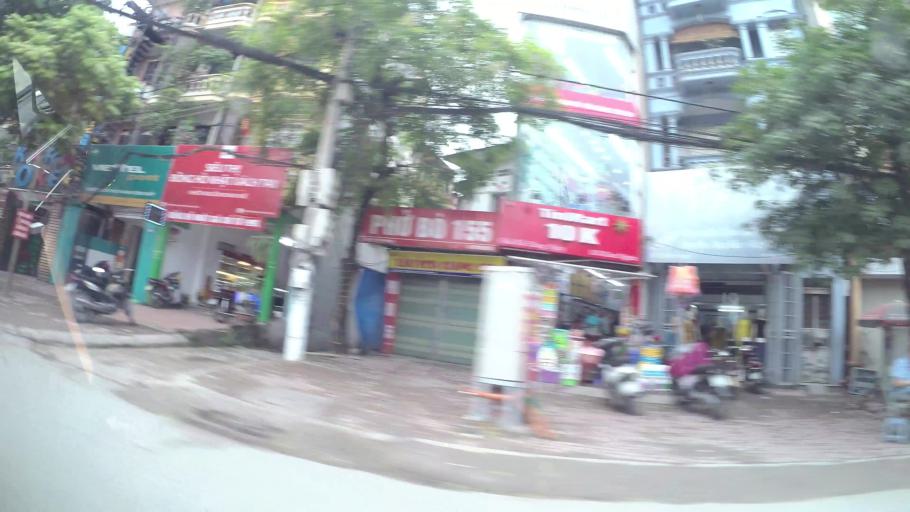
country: VN
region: Ha Noi
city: Hai BaTrung
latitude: 21.0072
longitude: 105.8613
